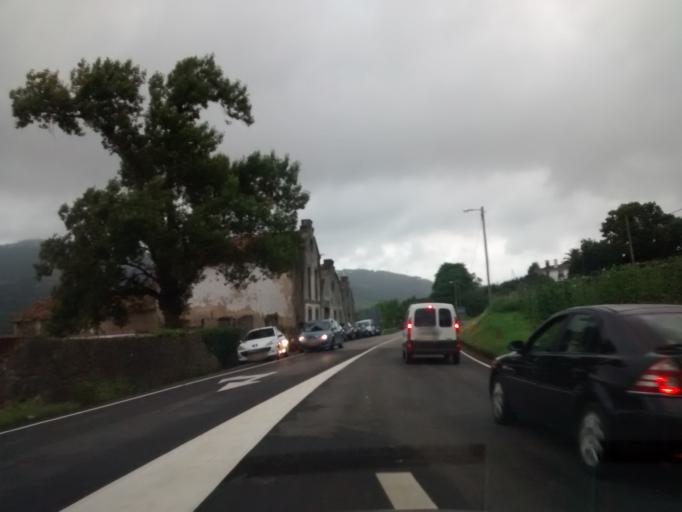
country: ES
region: Asturias
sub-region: Province of Asturias
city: Villaviciosa
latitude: 43.5004
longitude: -5.4267
